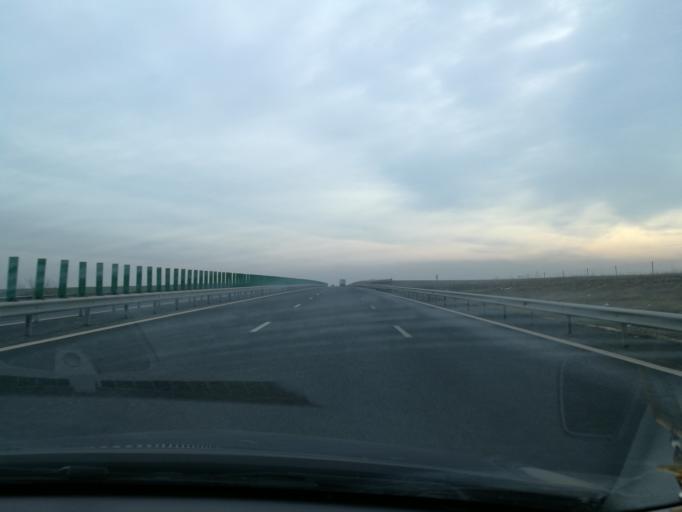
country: RO
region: Constanta
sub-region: Comuna Mircea Voda
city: Mircea Voda
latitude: 44.2386
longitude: 28.1436
